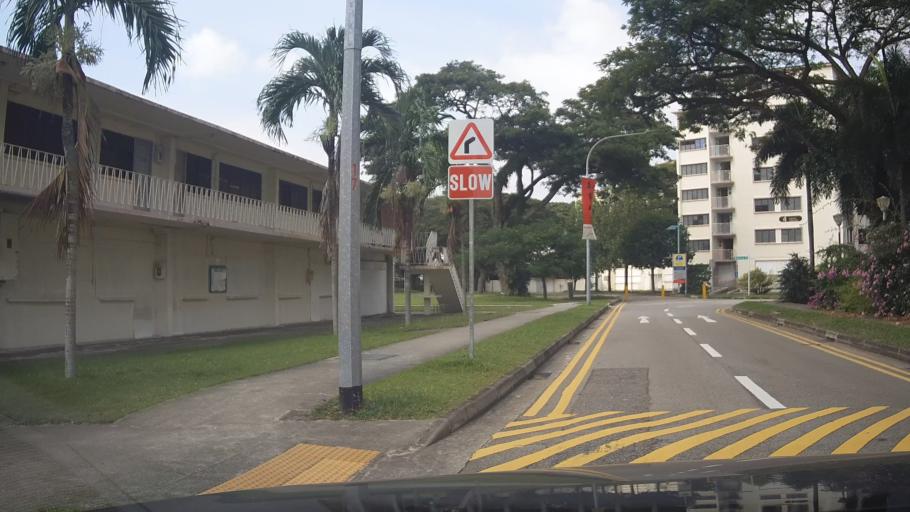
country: SG
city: Singapore
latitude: 1.3059
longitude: 103.8847
